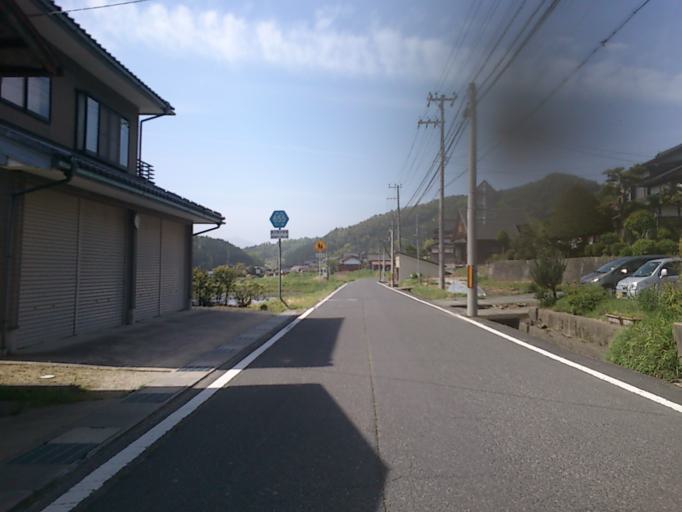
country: JP
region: Kyoto
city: Miyazu
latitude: 35.5666
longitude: 135.1147
